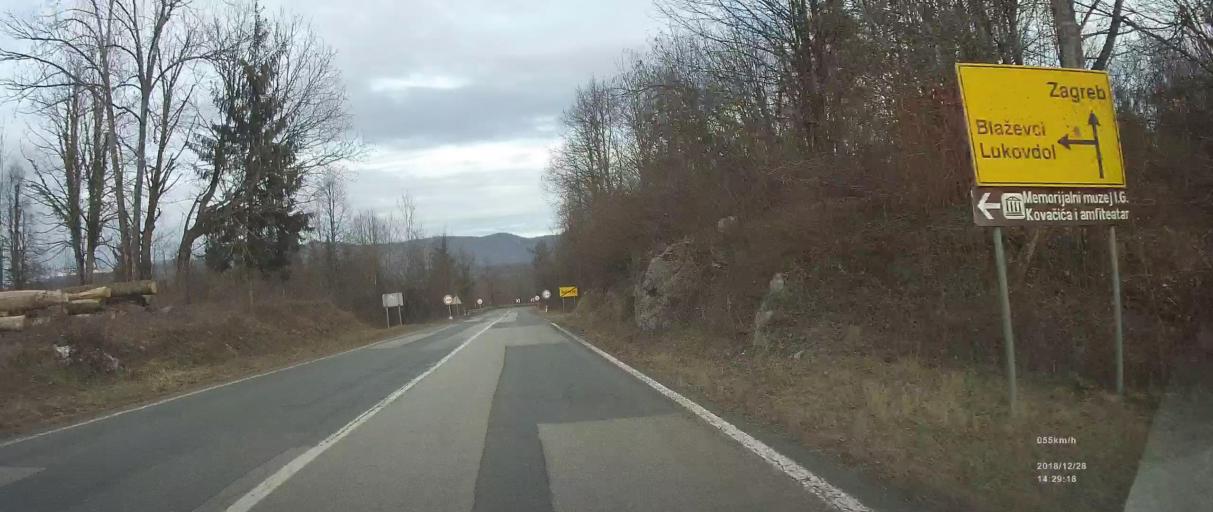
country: HR
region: Primorsko-Goranska
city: Vrbovsko
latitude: 45.4189
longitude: 15.1159
